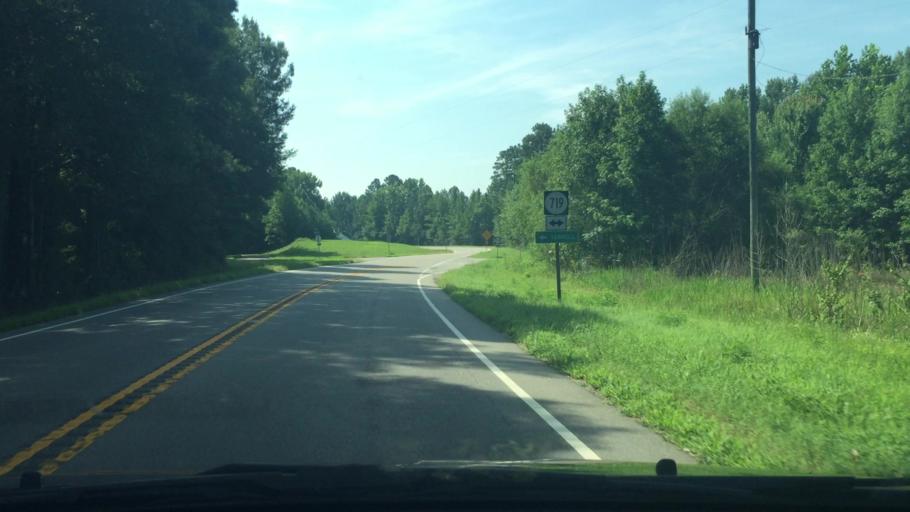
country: US
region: Virginia
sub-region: Southampton County
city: Courtland
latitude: 36.7880
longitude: -77.1281
